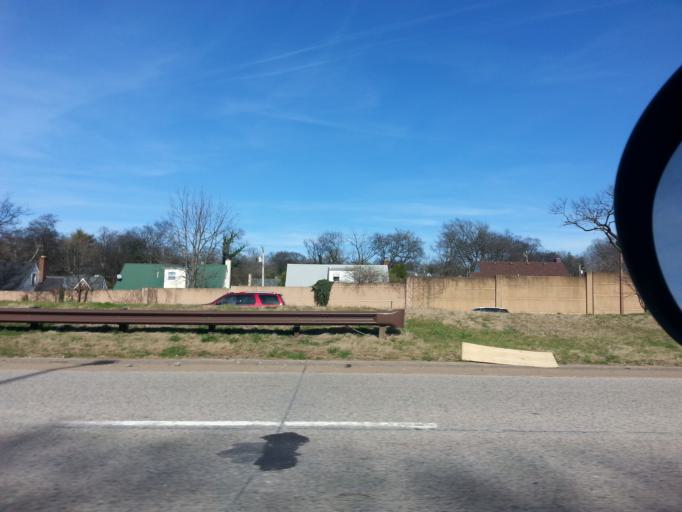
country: US
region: Tennessee
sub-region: Davidson County
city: Oak Hill
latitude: 36.1197
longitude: -86.8023
